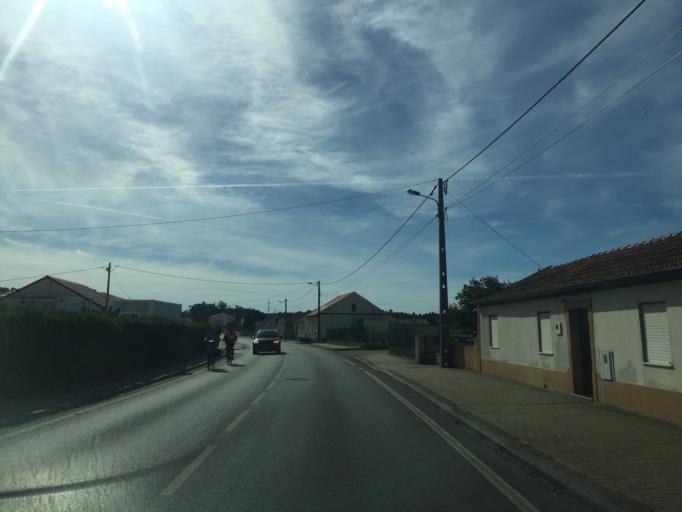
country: PT
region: Coimbra
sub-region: Figueira da Foz
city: Lavos
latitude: 40.0890
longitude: -8.8274
